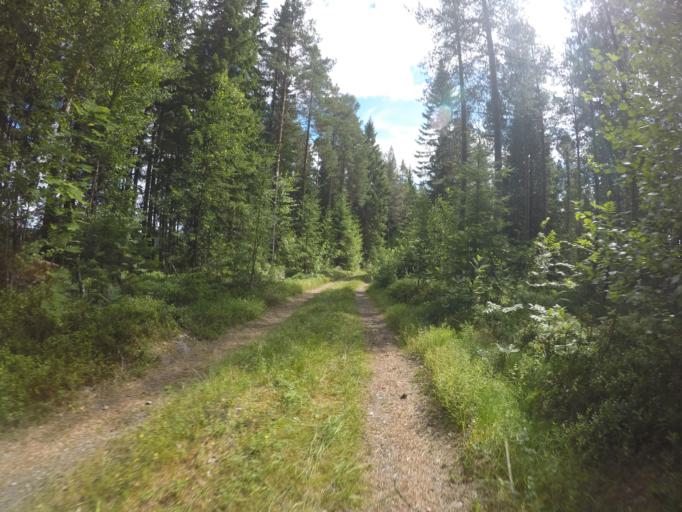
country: SE
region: Vaermland
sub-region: Filipstads Kommun
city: Lesjofors
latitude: 60.0787
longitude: 14.4573
